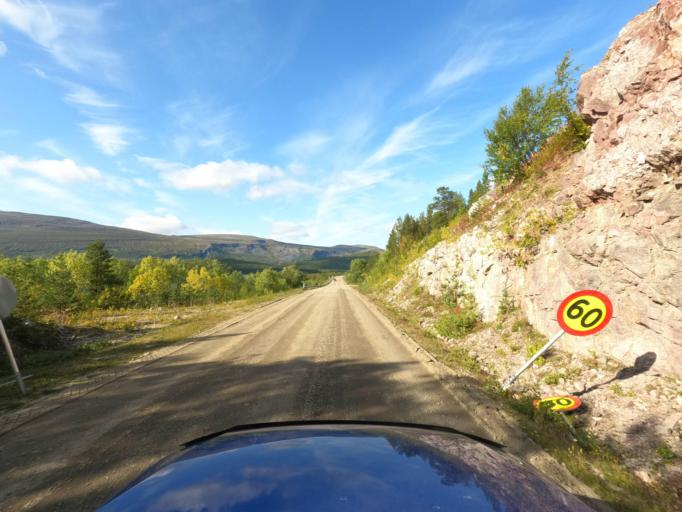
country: NO
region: Finnmark Fylke
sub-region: Porsanger
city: Lakselv
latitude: 69.8907
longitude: 25.0013
